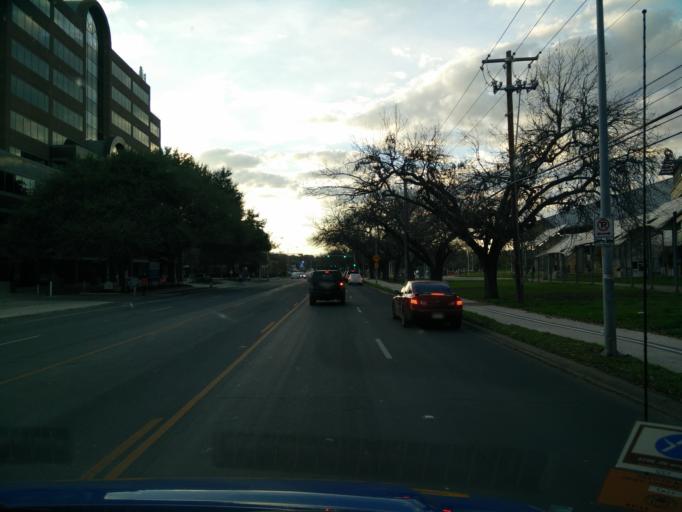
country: US
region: Texas
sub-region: Travis County
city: Austin
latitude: 30.2592
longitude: -97.7521
